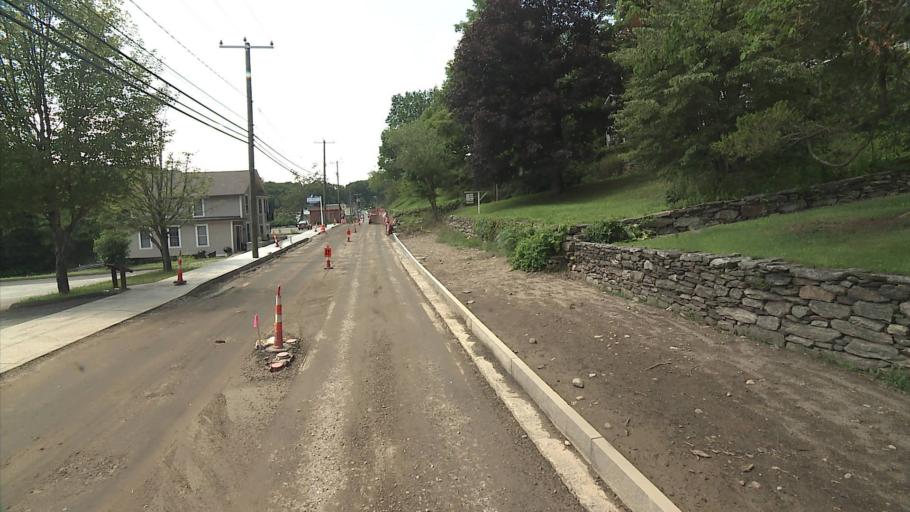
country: US
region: Connecticut
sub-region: Tolland County
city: South Coventry
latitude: 41.7680
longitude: -72.3000
